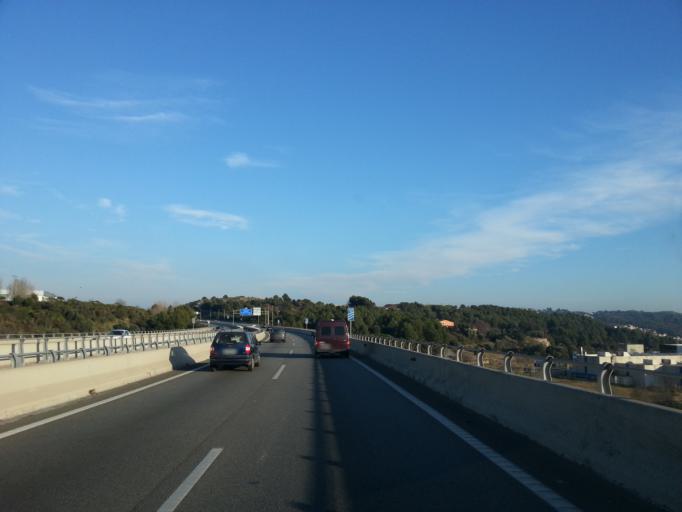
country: ES
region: Catalonia
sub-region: Provincia de Barcelona
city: Terrassa
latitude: 41.5422
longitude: 2.0200
